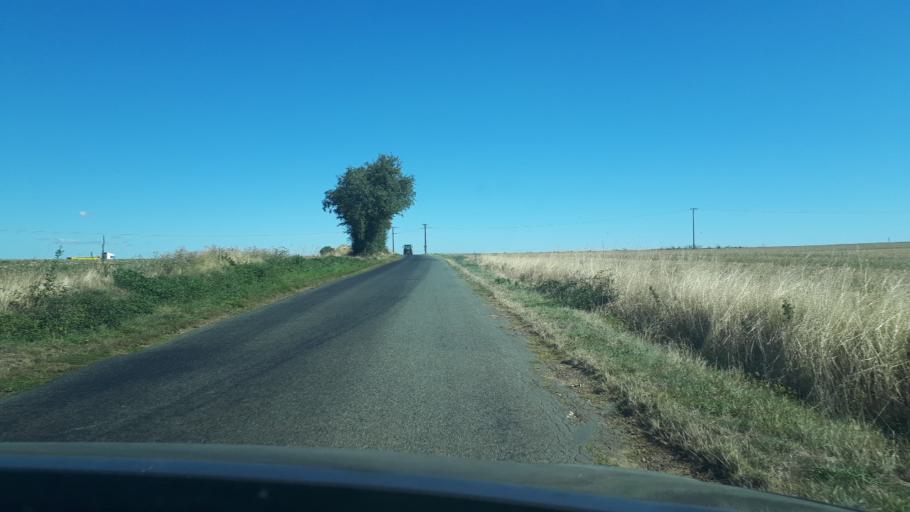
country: FR
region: Centre
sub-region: Departement du Cher
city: Sancerre
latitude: 47.3239
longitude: 2.7752
